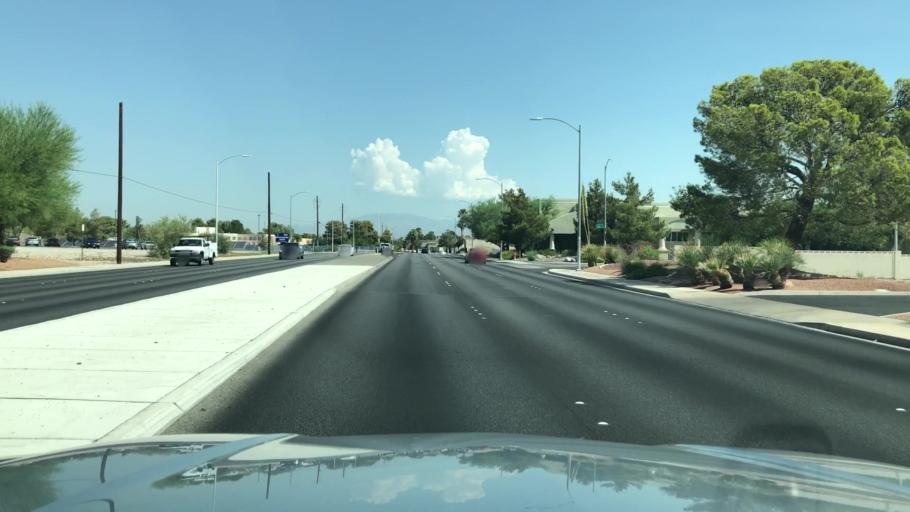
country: US
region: Nevada
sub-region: Clark County
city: Spring Valley
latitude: 36.1531
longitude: -115.2256
